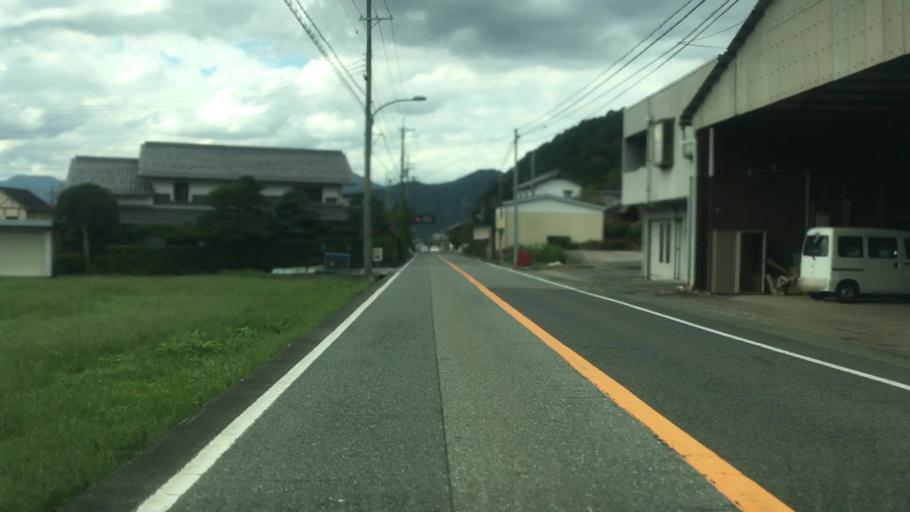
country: JP
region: Kyoto
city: Fukuchiyama
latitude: 35.3074
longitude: 134.9045
